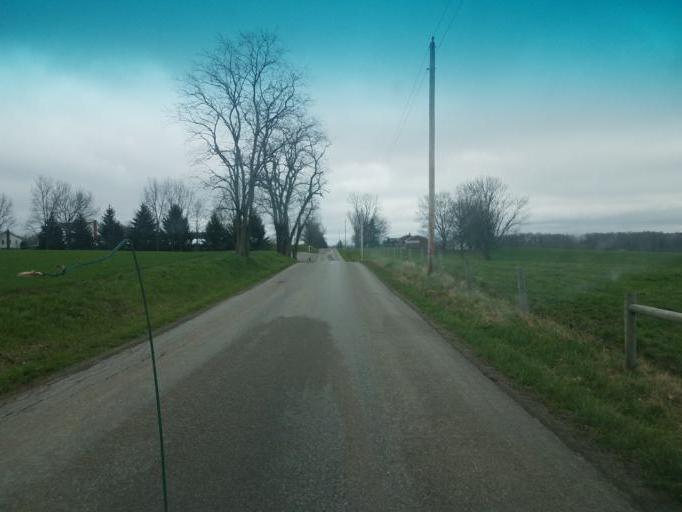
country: US
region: Ohio
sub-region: Stark County
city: Beach City
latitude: 40.6191
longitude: -81.6837
